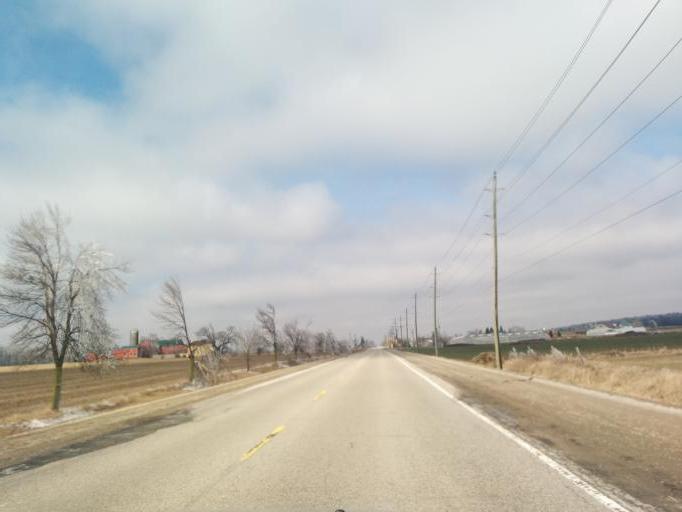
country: CA
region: Ontario
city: Waterloo
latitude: 43.6275
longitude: -80.5509
